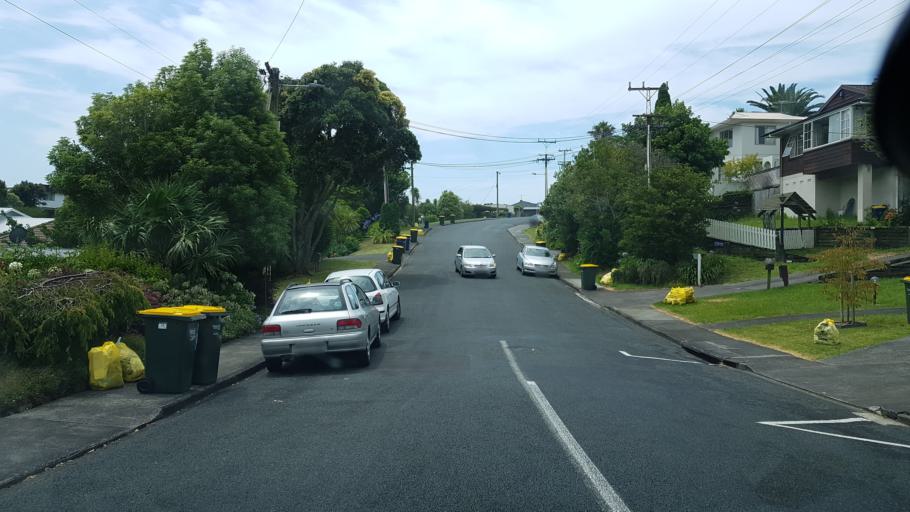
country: NZ
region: Auckland
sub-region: Auckland
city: North Shore
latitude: -36.7988
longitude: 174.7760
